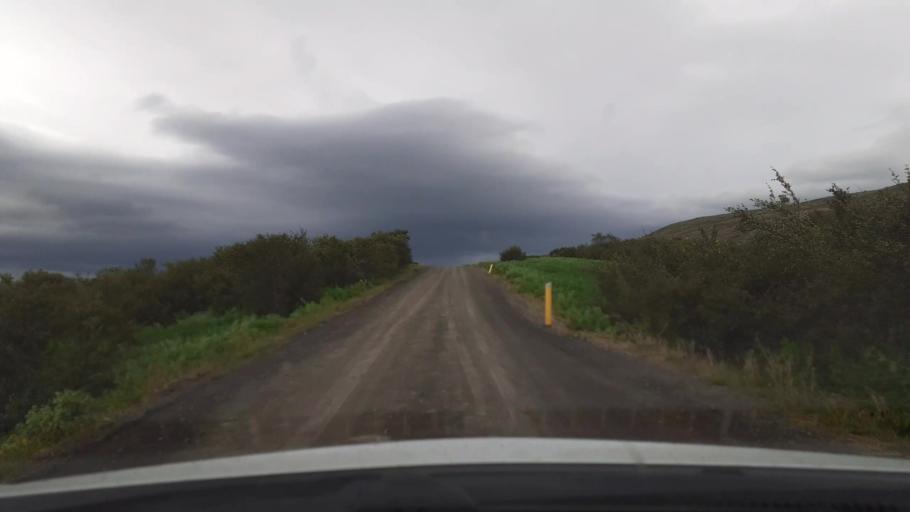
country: IS
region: Capital Region
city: Mosfellsbaer
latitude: 64.5243
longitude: -21.4753
